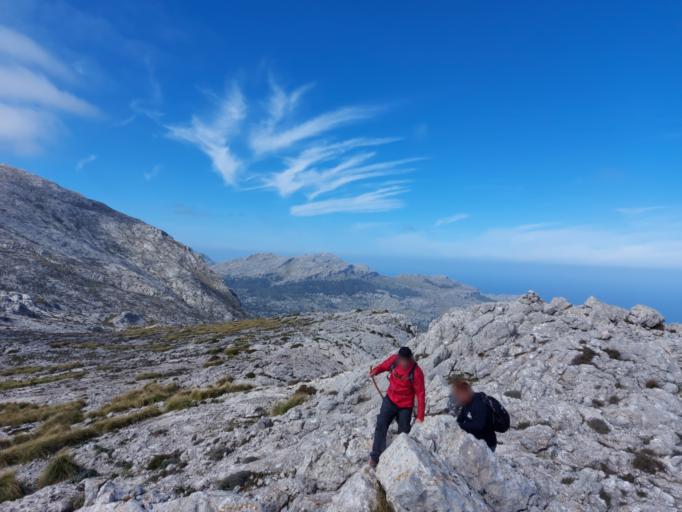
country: ES
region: Balearic Islands
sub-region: Illes Balears
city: Campanet
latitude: 39.8437
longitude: 2.9458
